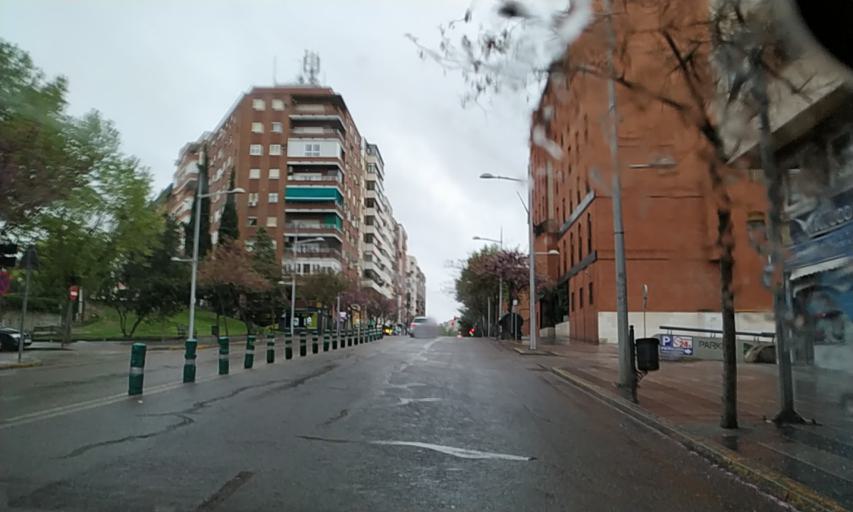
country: ES
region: Extremadura
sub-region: Provincia de Badajoz
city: Badajoz
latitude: 38.8726
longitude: -6.9729
